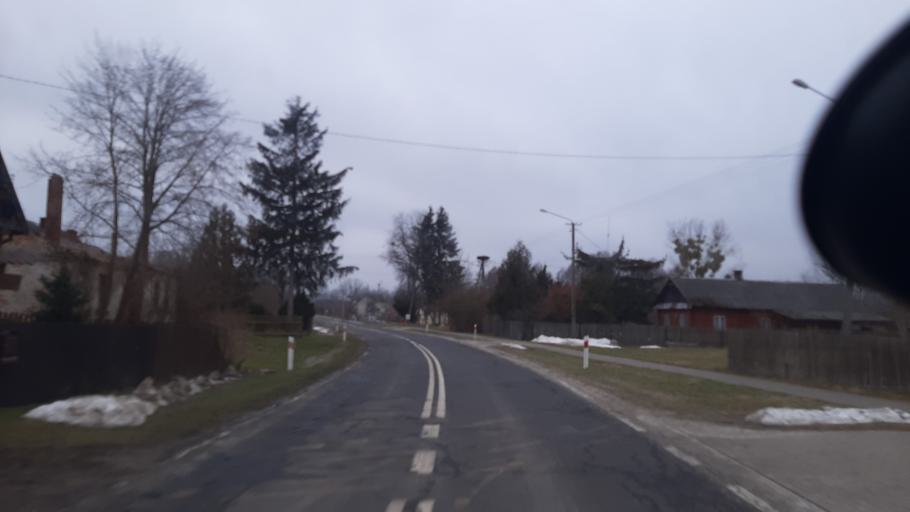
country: PL
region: Lublin Voivodeship
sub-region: Powiat wlodawski
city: Hansk
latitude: 51.5628
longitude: 23.3810
